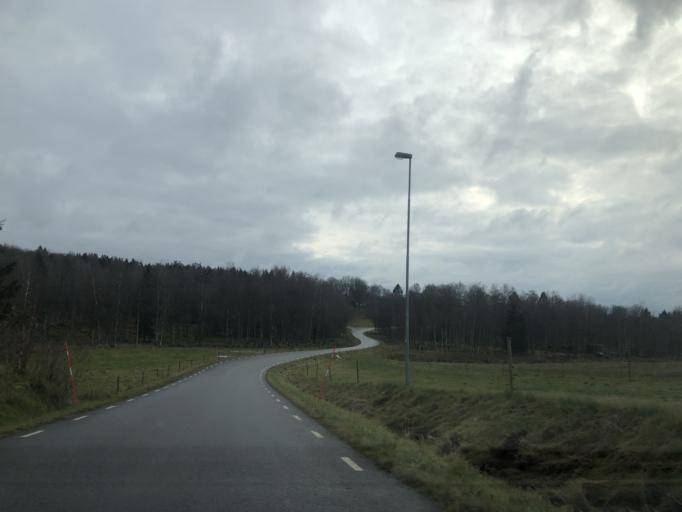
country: SE
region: Vaestra Goetaland
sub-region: Ulricehamns Kommun
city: Ulricehamn
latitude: 57.8226
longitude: 13.2452
